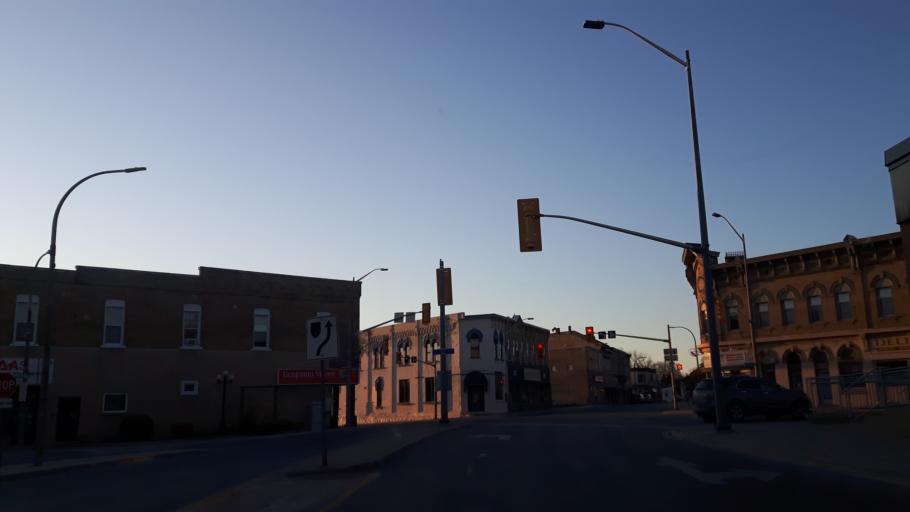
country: CA
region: Ontario
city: Bluewater
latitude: 43.6167
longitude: -81.5395
